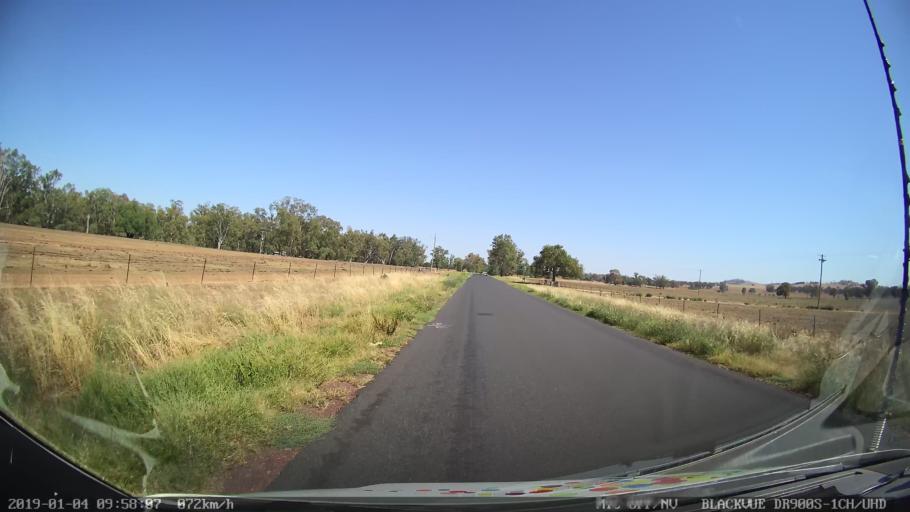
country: AU
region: New South Wales
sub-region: Cabonne
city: Canowindra
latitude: -33.5216
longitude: 148.3969
